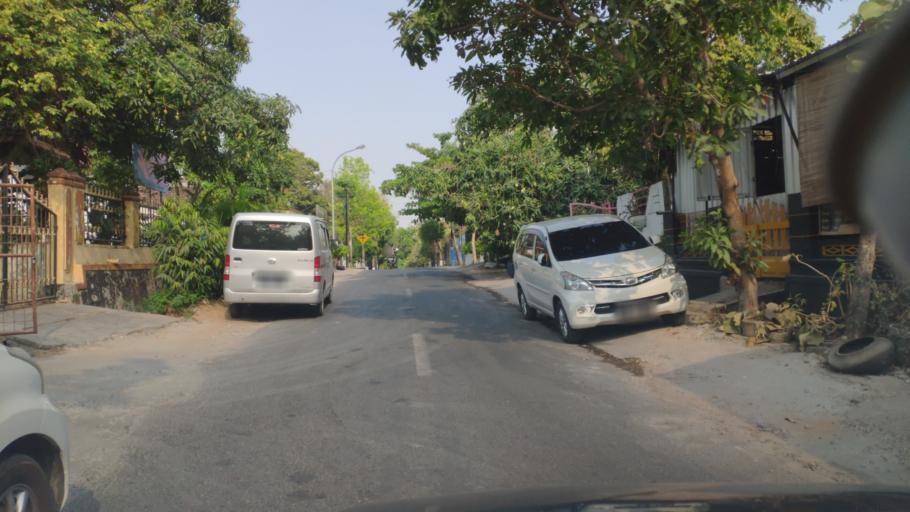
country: ID
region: Central Java
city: Kunden
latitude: -6.9638
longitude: 111.4136
